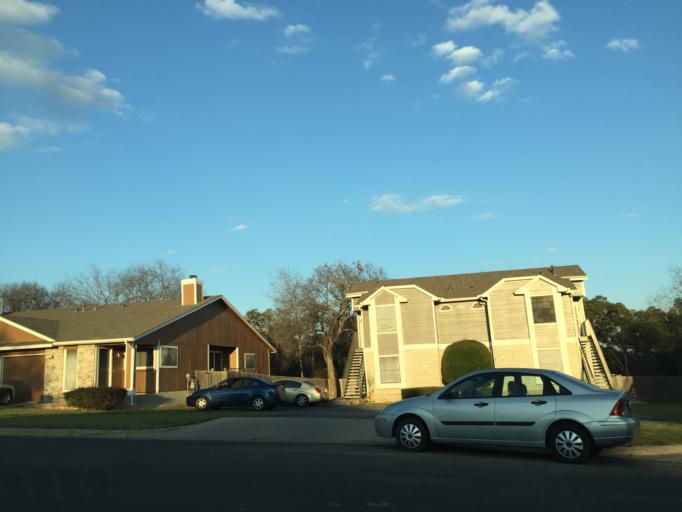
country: US
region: Texas
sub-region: Williamson County
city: Jollyville
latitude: 30.4381
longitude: -97.7460
